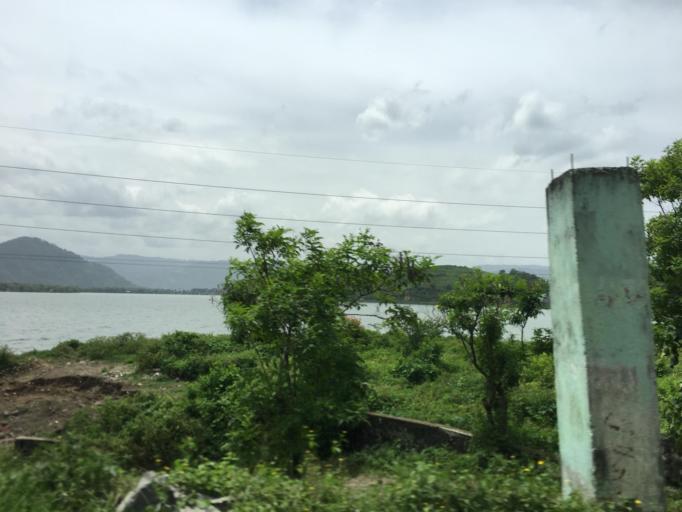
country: GT
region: Guatemala
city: Amatitlan
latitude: 14.4668
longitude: -90.5892
